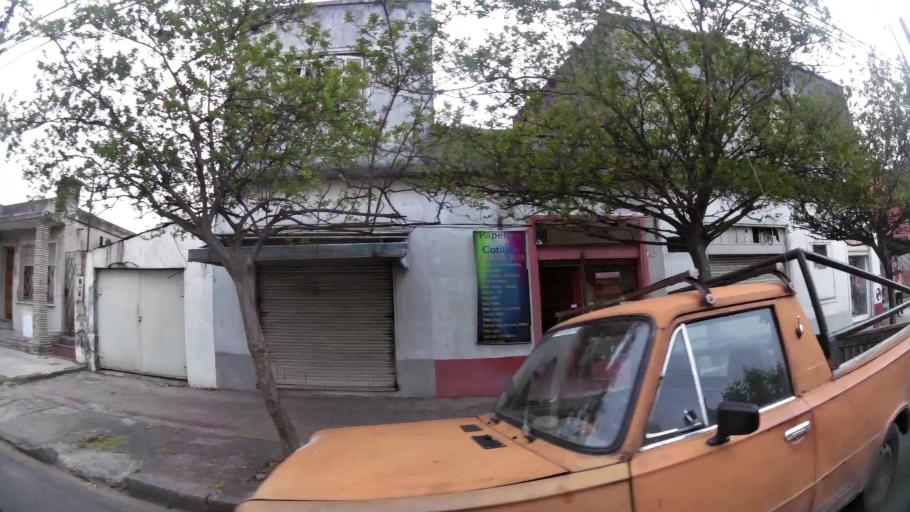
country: AR
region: Buenos Aires
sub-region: Partido de Avellaneda
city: Avellaneda
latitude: -34.6562
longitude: -58.3547
